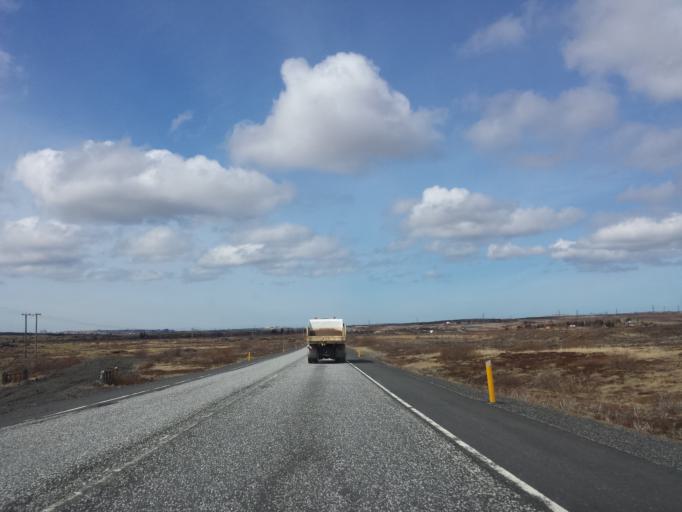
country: IS
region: Capital Region
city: Mosfellsbaer
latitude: 64.0785
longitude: -21.6588
